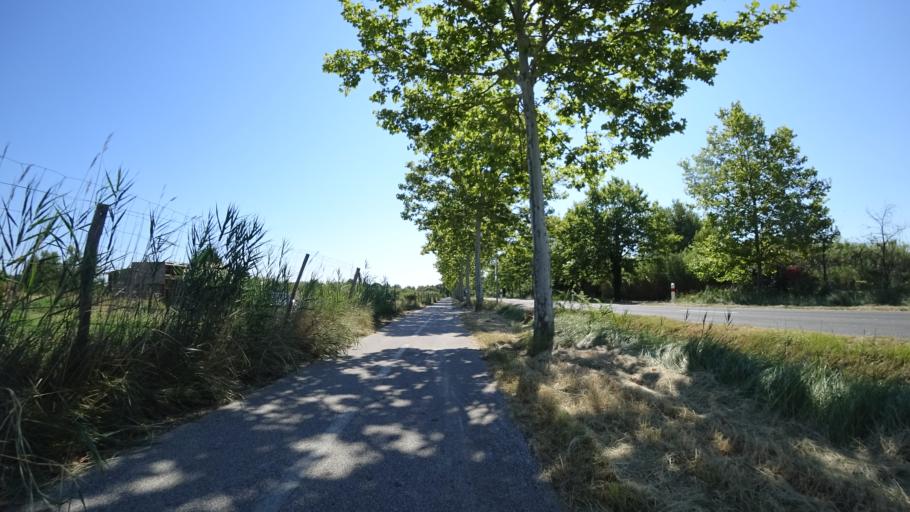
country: FR
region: Languedoc-Roussillon
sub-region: Departement des Pyrenees-Orientales
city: Villelongue-de-la-Salanque
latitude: 42.7272
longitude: 3.0051
